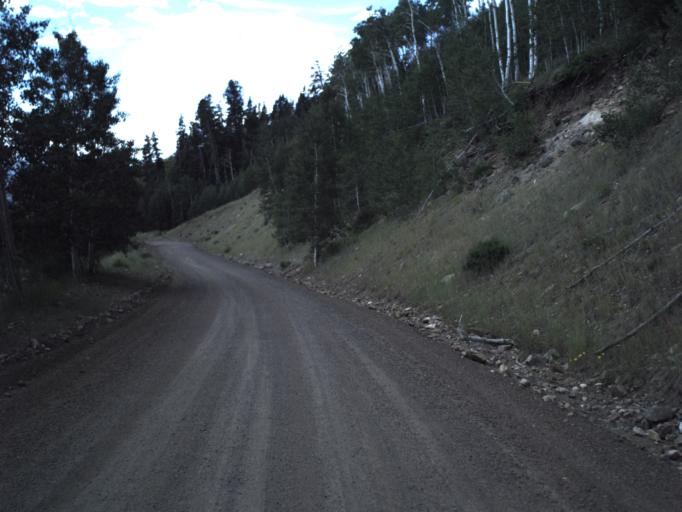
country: US
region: Utah
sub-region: Piute County
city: Junction
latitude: 38.2564
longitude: -112.3277
